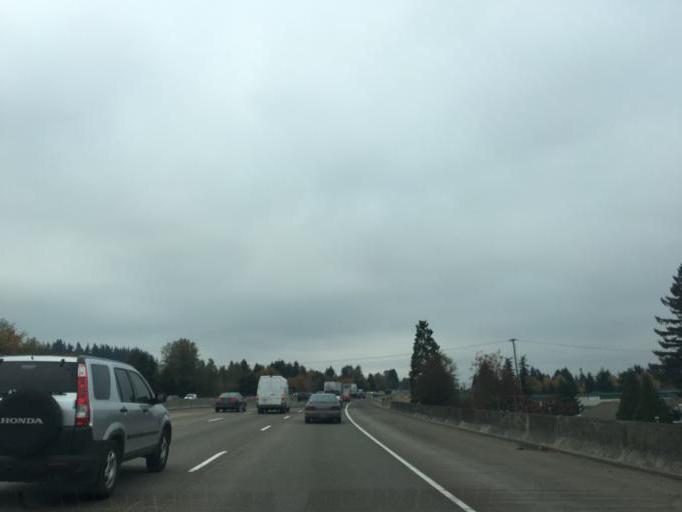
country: US
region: Oregon
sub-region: Multnomah County
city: Lents
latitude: 45.4687
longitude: -122.5659
